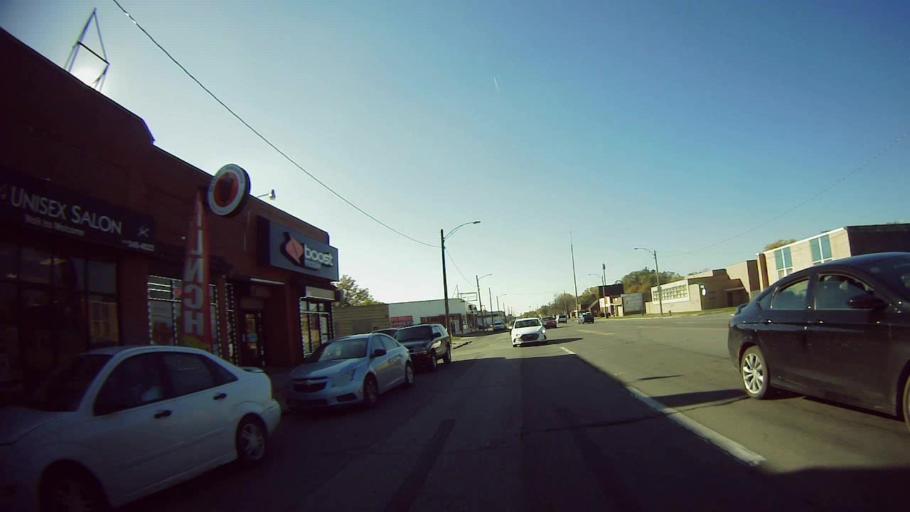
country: US
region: Michigan
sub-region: Oakland County
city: Oak Park
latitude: 42.4312
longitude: -83.1712
